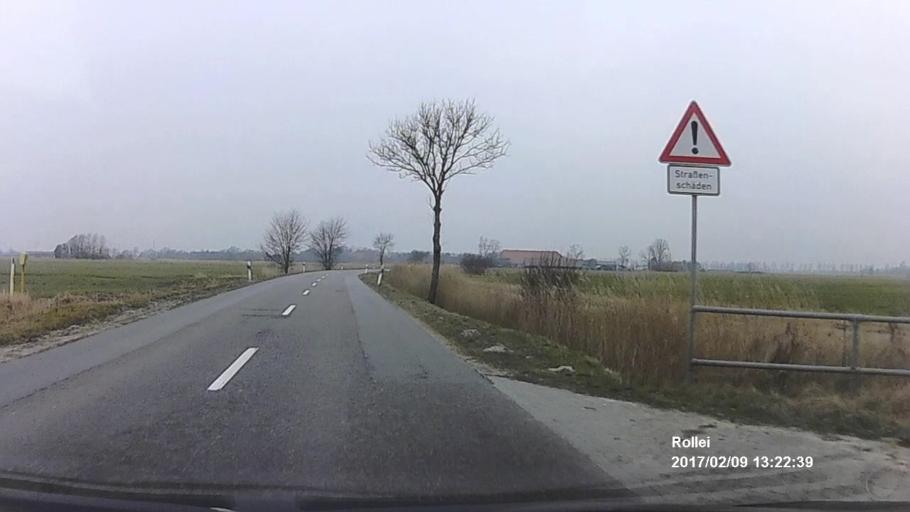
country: DE
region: Lower Saxony
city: Hinte
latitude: 53.4573
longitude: 7.1473
